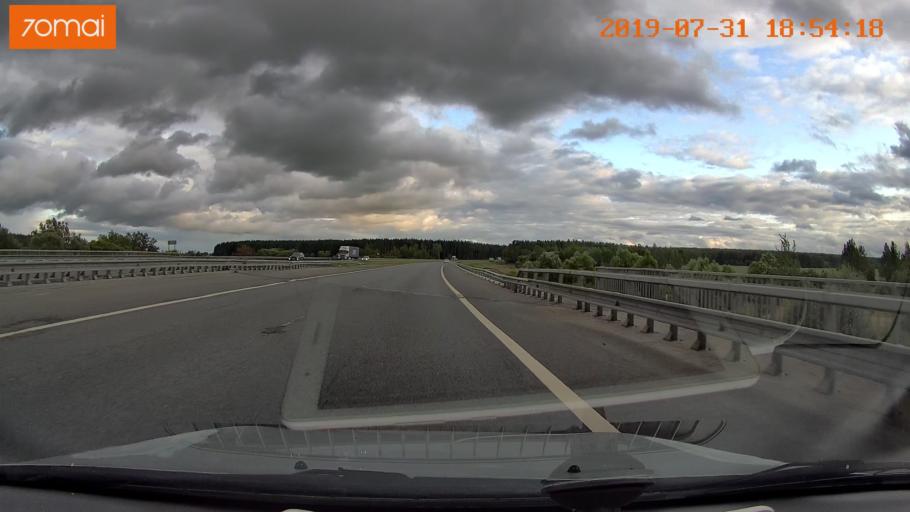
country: RU
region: Moskovskaya
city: Raduzhnyy
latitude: 55.1921
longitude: 38.6675
